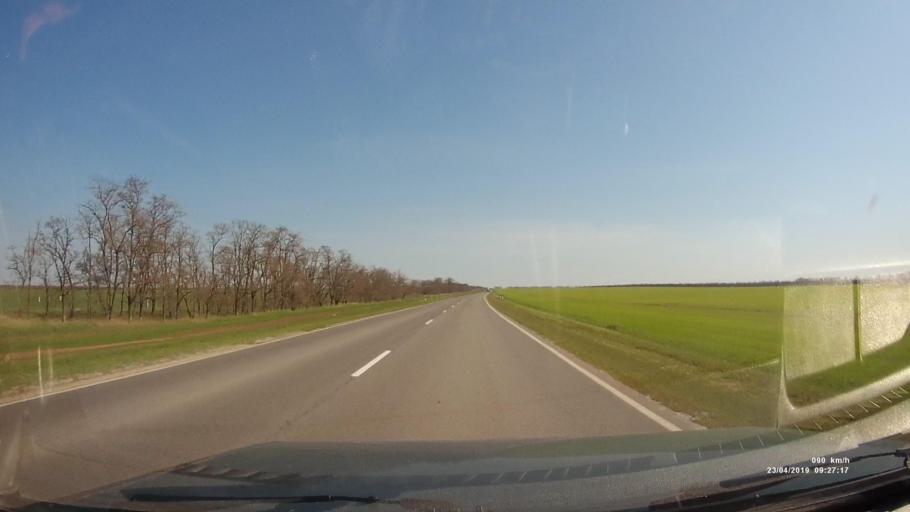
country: RU
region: Rostov
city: Proletarsk
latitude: 46.7376
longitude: 41.7793
